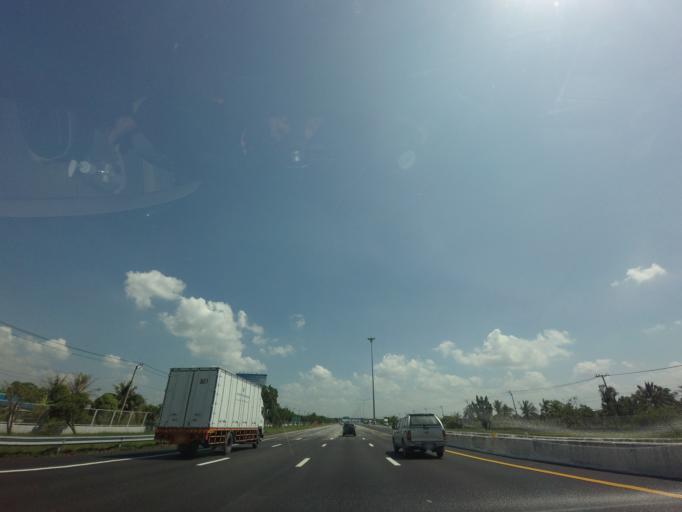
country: TH
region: Samut Prakan
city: Ban Khlong Bang Sao Thong
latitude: 13.6194
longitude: 100.9228
